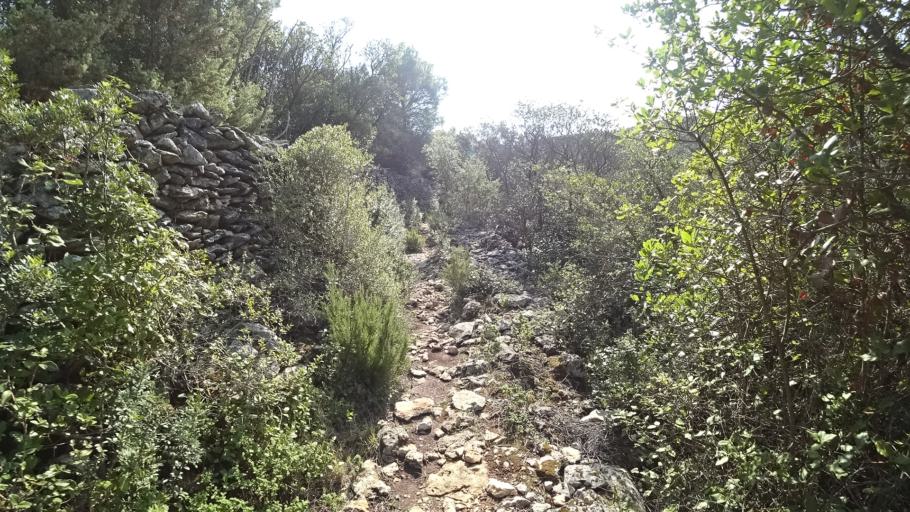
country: HR
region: Primorsko-Goranska
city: Mali Losinj
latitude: 44.5007
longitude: 14.5239
